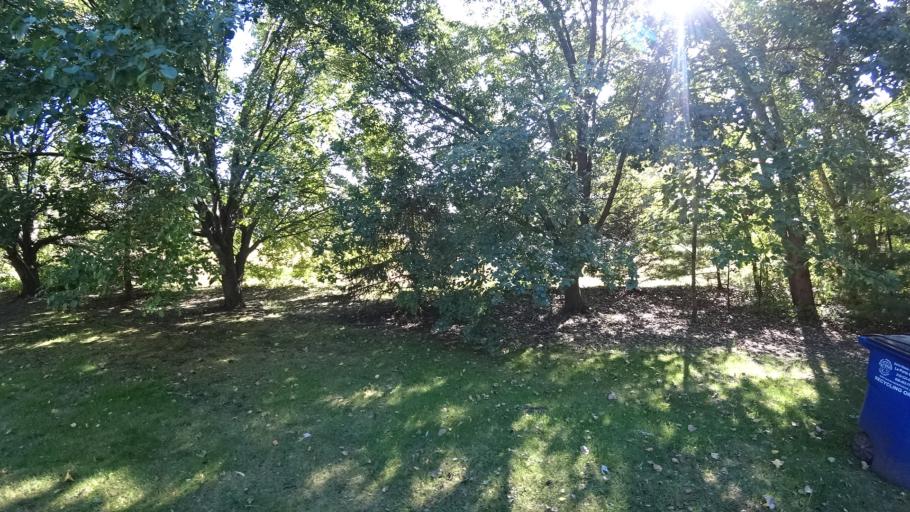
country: US
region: Indiana
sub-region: LaPorte County
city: Trail Creek
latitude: 41.7004
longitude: -86.8281
